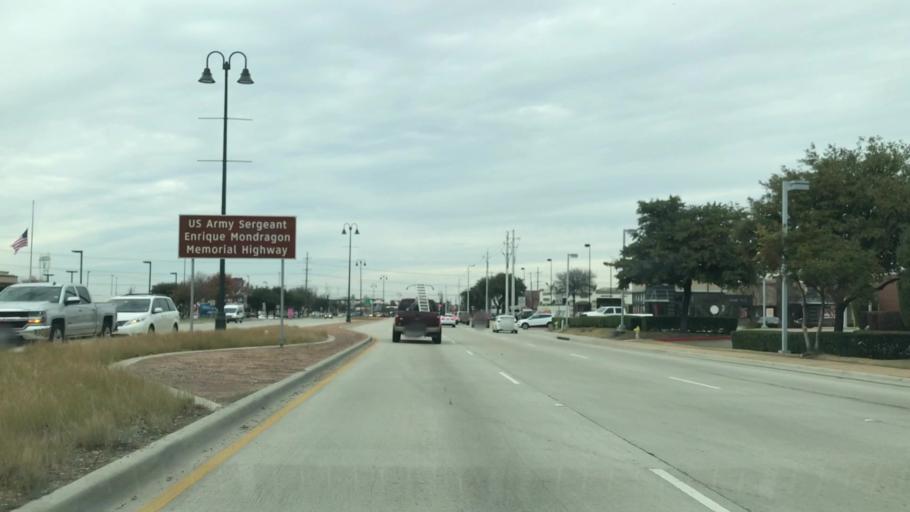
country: US
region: Texas
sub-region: Denton County
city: The Colony
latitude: 33.0664
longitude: -96.8892
